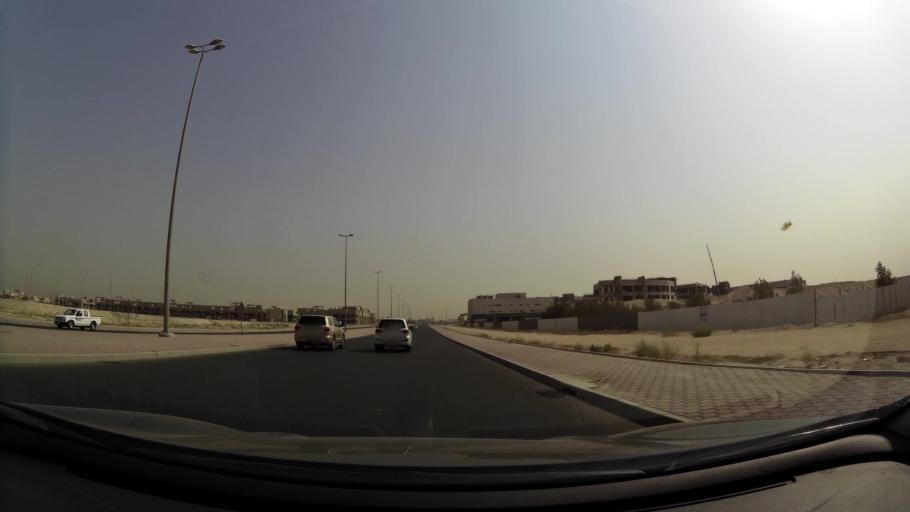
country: KW
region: Al Asimah
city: Ar Rabiyah
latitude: 29.2887
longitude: 47.9076
